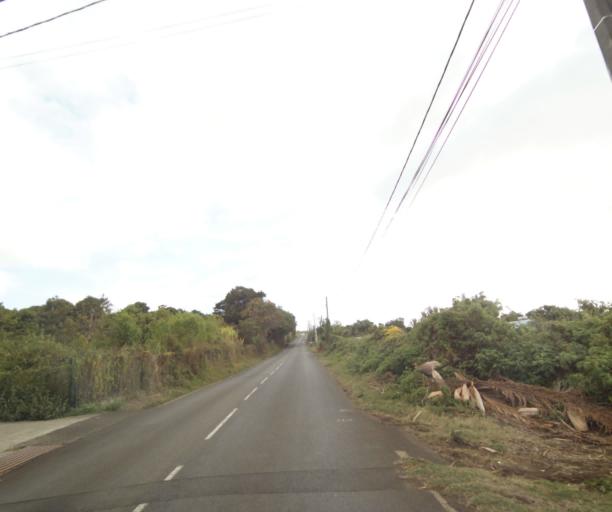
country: RE
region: Reunion
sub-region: Reunion
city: Trois-Bassins
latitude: -21.0593
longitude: 55.2819
